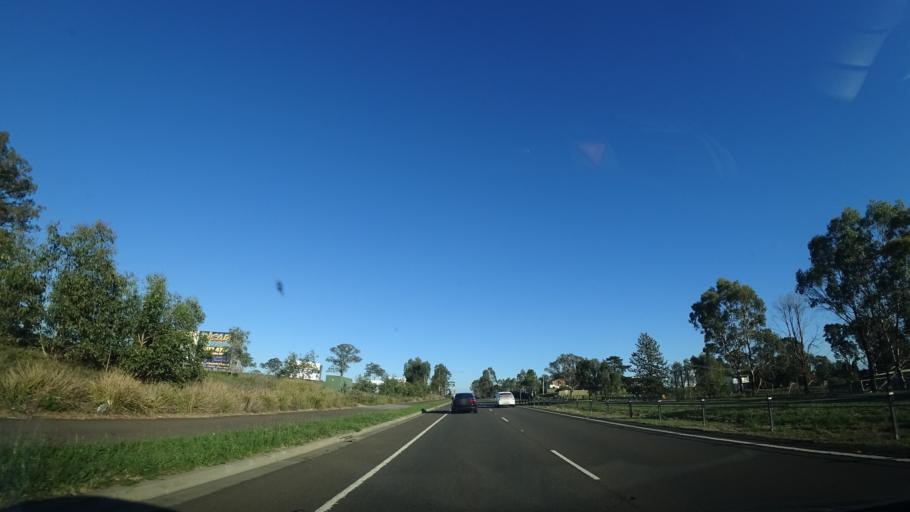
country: AU
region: New South Wales
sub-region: Blacktown
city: Rouse Hill
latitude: -33.6644
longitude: 150.8970
